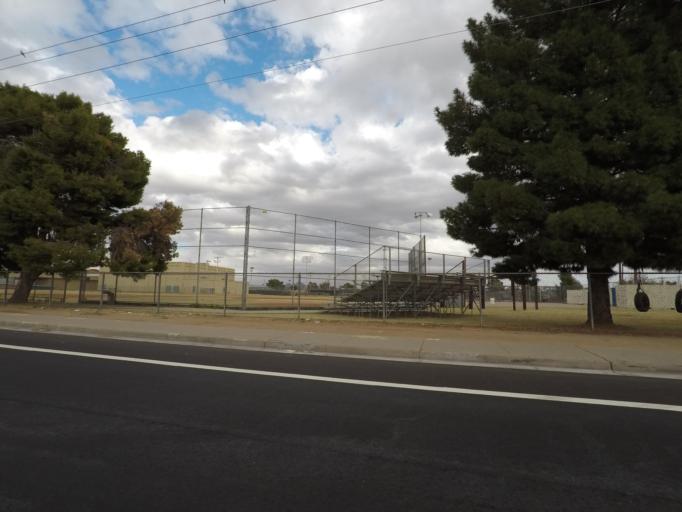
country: US
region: Arizona
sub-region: Maricopa County
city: Glendale
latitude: 33.5061
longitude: -112.1429
